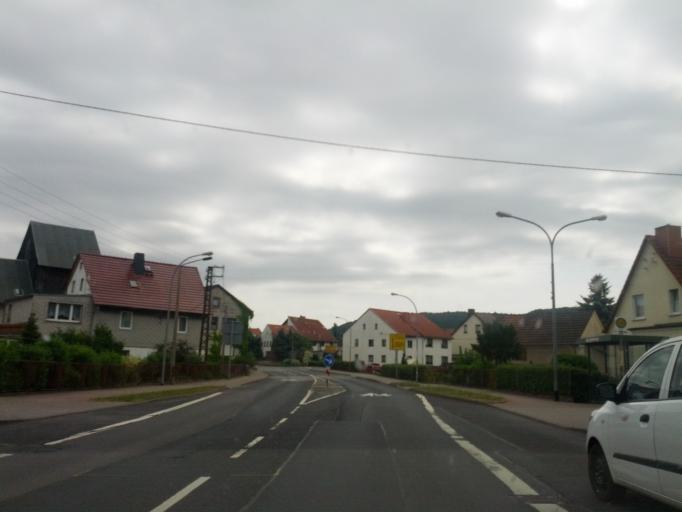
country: DE
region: Thuringia
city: Dorndorf
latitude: 50.8380
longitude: 10.0824
